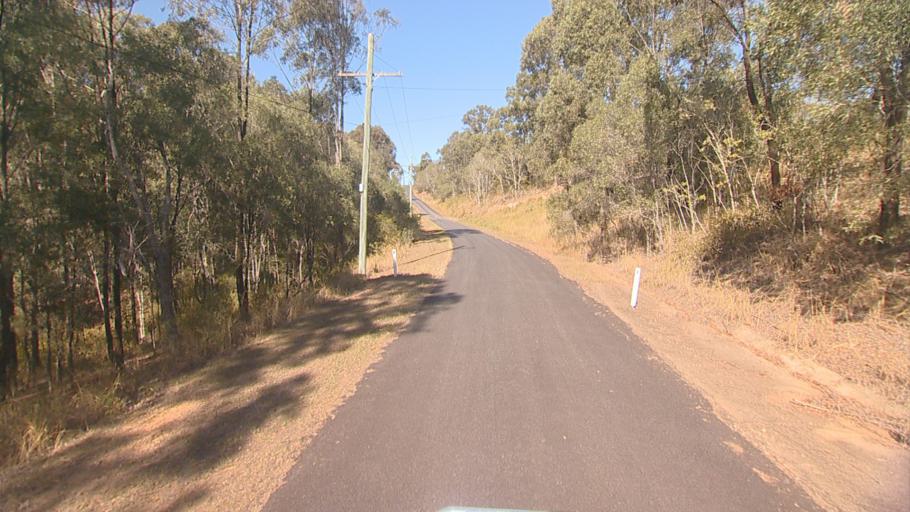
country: AU
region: Queensland
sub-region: Logan
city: Cedar Vale
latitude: -27.8981
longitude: 153.0215
